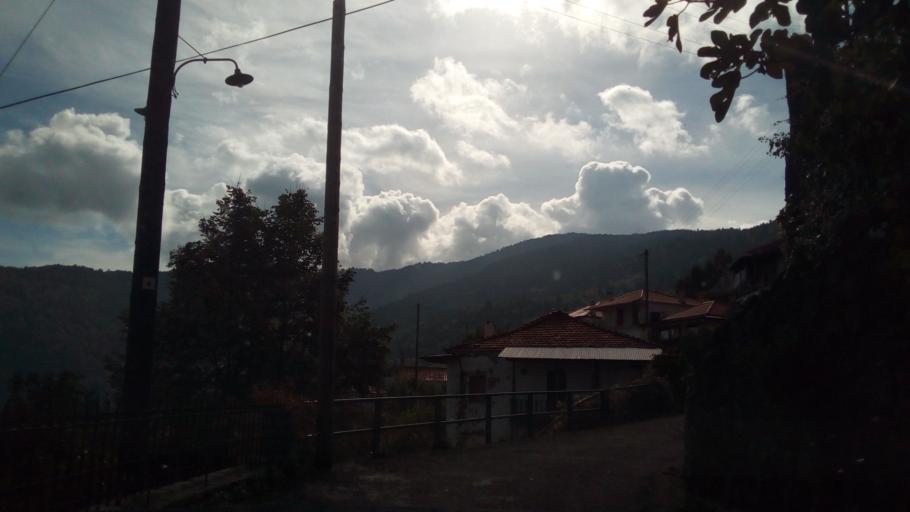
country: GR
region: Central Greece
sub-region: Nomos Fokidos
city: Lidoriki
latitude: 38.4884
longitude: 22.0556
